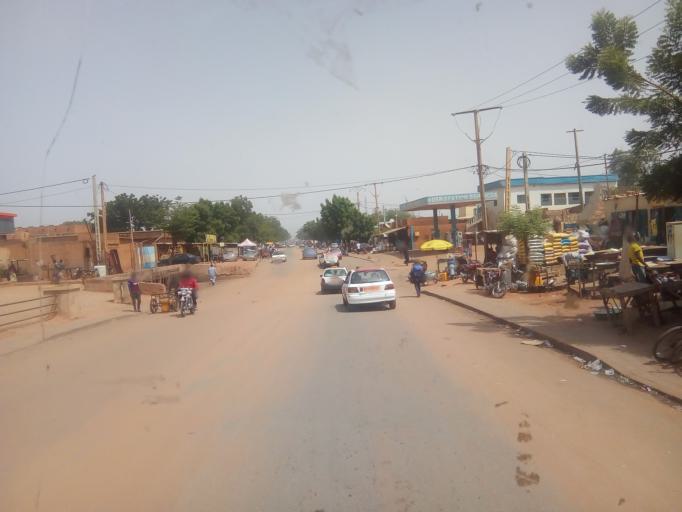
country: NE
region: Niamey
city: Niamey
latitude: 13.5256
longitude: 2.1210
